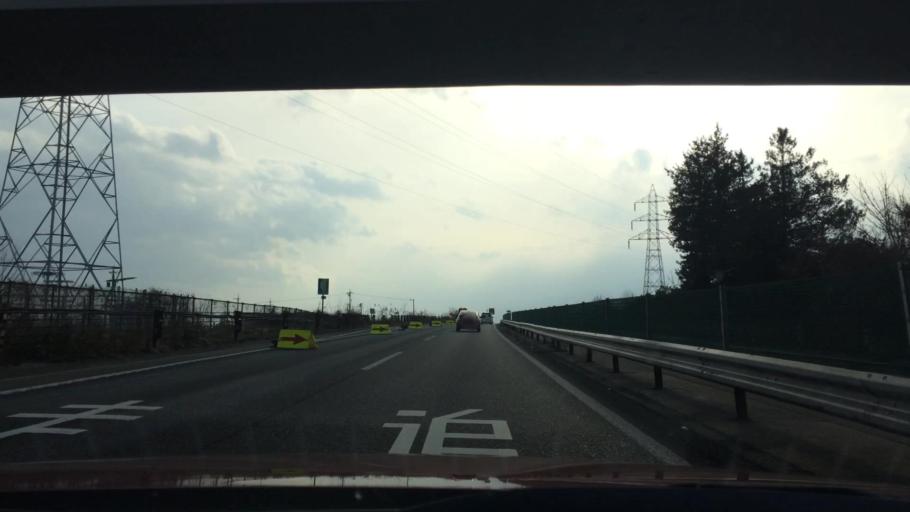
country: JP
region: Nagano
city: Tatsuno
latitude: 35.9195
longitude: 137.9692
